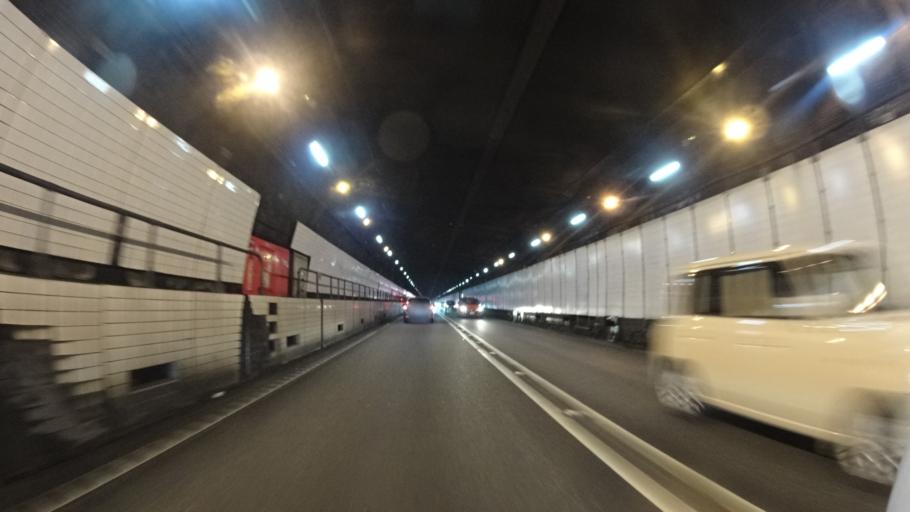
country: JP
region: Yamaguchi
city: Shimonoseki
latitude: 33.9745
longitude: 130.9479
